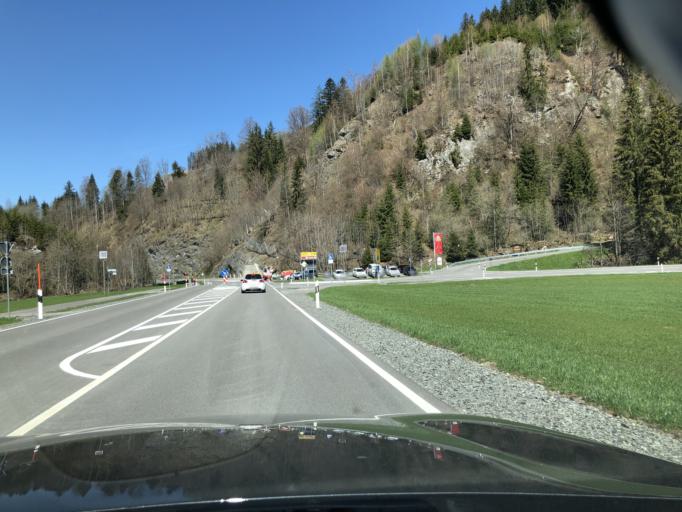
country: DE
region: Bavaria
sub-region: Swabia
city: Wertach
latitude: 47.5805
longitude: 10.4213
